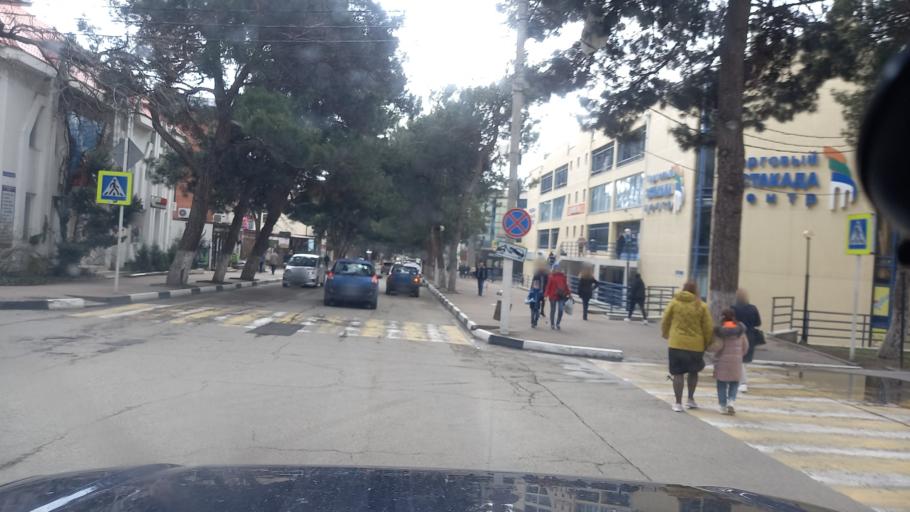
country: RU
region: Krasnodarskiy
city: Gelendzhik
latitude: 44.5639
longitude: 38.0821
